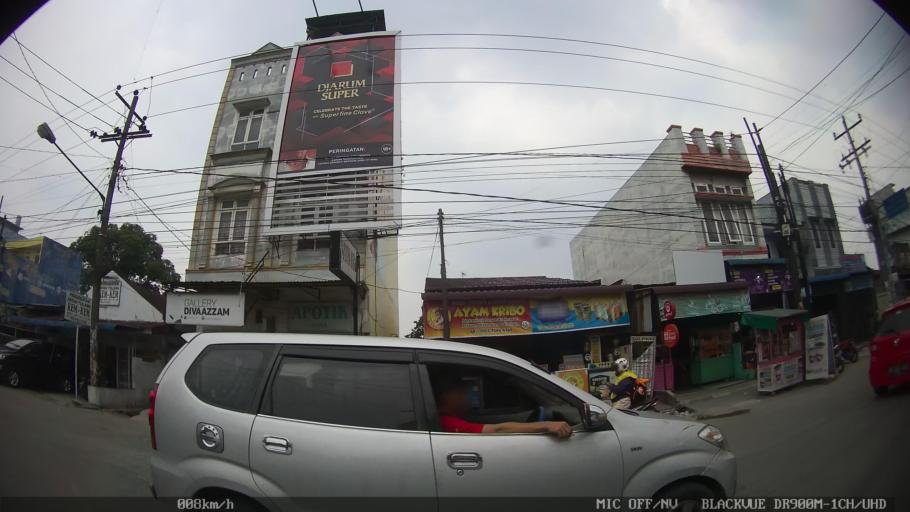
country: ID
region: North Sumatra
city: Medan
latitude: 3.5819
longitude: 98.7110
